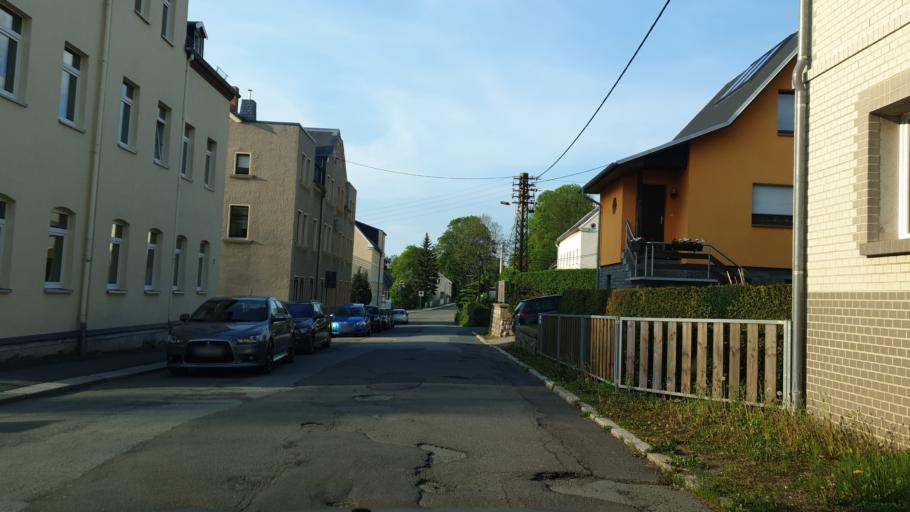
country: DE
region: Saxony
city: Stollberg
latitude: 50.7129
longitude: 12.7861
